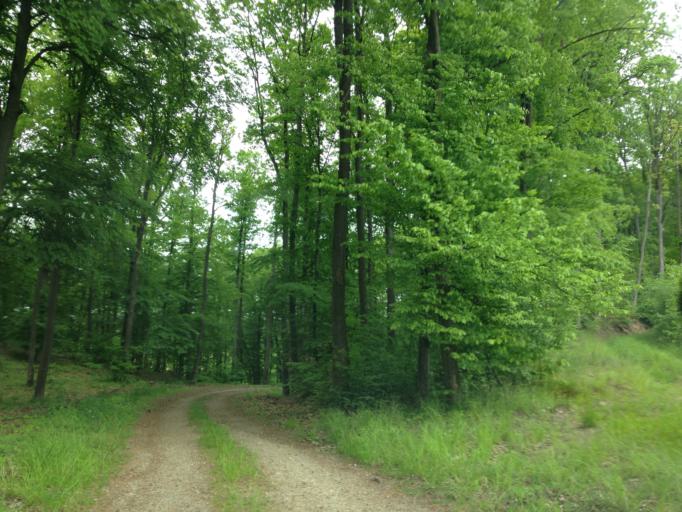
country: PL
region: Kujawsko-Pomorskie
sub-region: Powiat brodnicki
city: Gorzno
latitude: 53.2622
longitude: 19.7109
